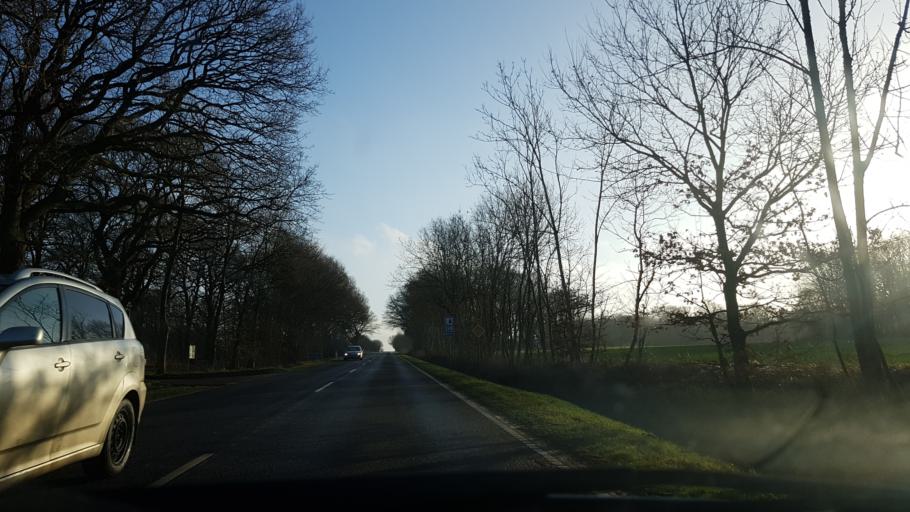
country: DK
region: South Denmark
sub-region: Tonder Kommune
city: Toftlund
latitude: 55.2220
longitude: 9.1778
